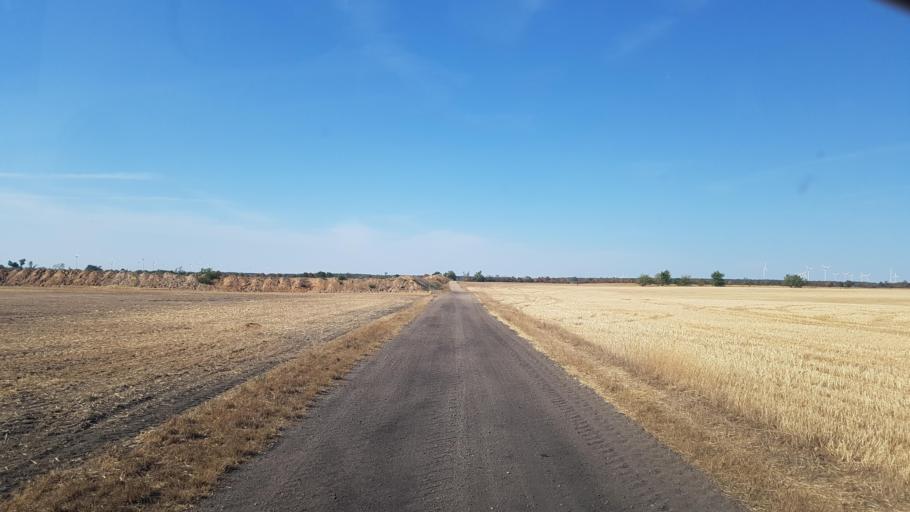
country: DE
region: Brandenburg
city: Muhlberg
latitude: 51.4169
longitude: 13.2866
